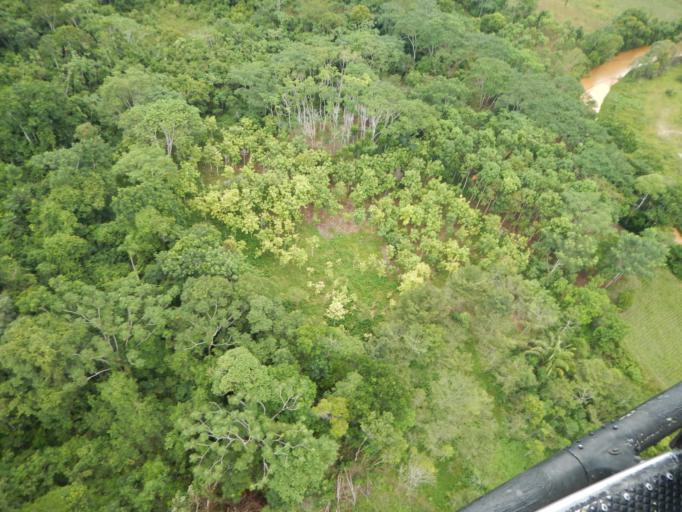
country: BO
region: Cochabamba
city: Chimore
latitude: -17.0052
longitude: -65.0077
